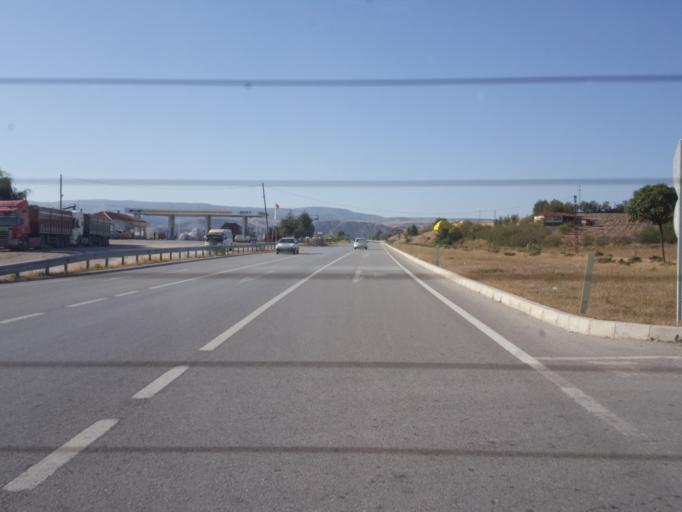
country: TR
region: Amasya
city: Saribugday
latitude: 40.7511
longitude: 35.4476
